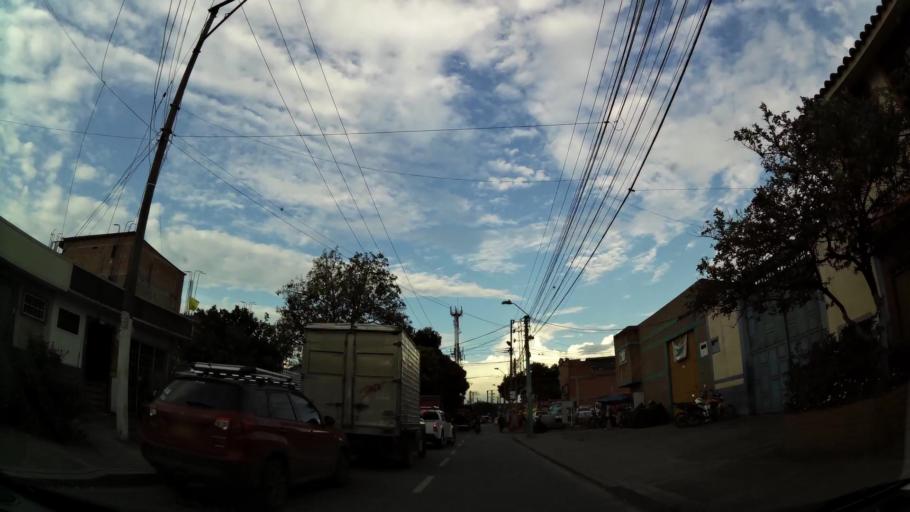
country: CO
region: Valle del Cauca
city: Cali
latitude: 3.4569
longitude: -76.5144
